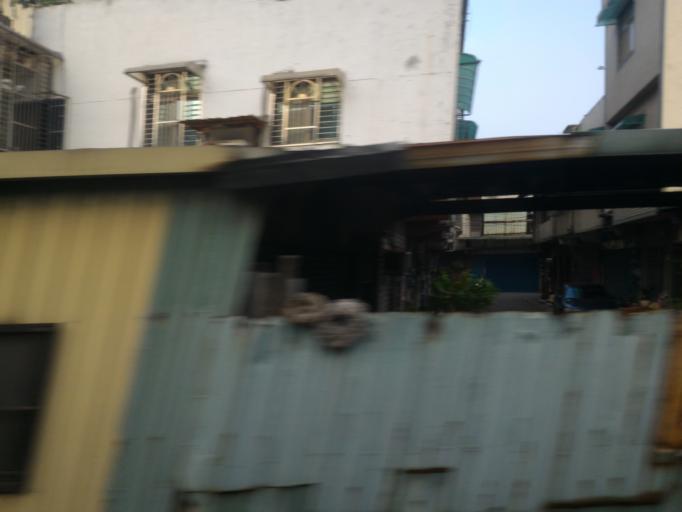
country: TW
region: Taiwan
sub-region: Taoyuan
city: Taoyuan
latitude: 24.9790
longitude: 121.3301
